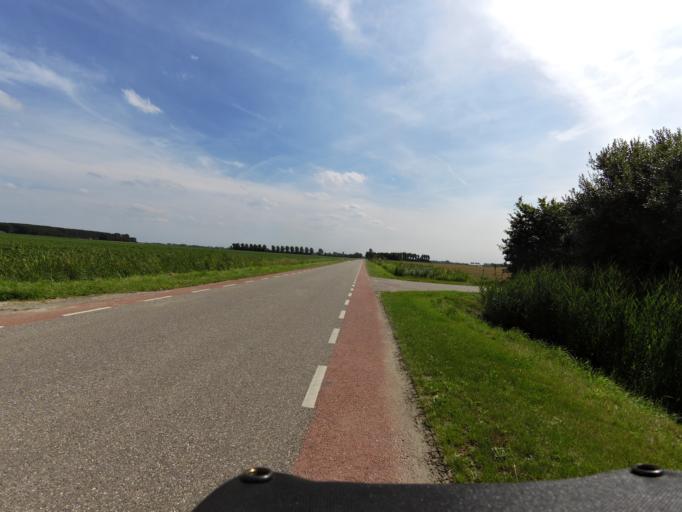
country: NL
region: South Holland
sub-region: Gemeente Goeree-Overflakkee
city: Middelharnis
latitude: 51.7427
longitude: 4.1523
